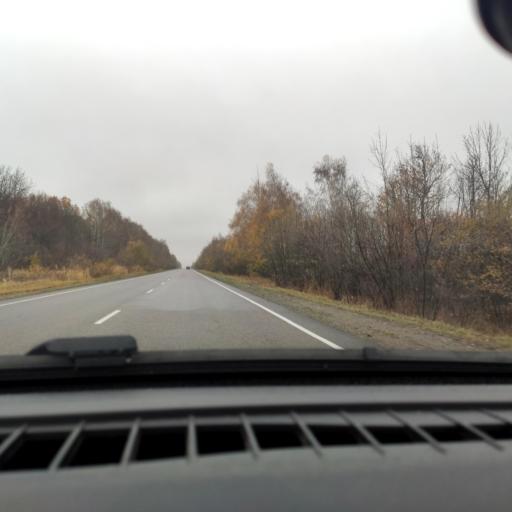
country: RU
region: Voronezj
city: Kolodeznyy
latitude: 51.3542
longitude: 39.0237
